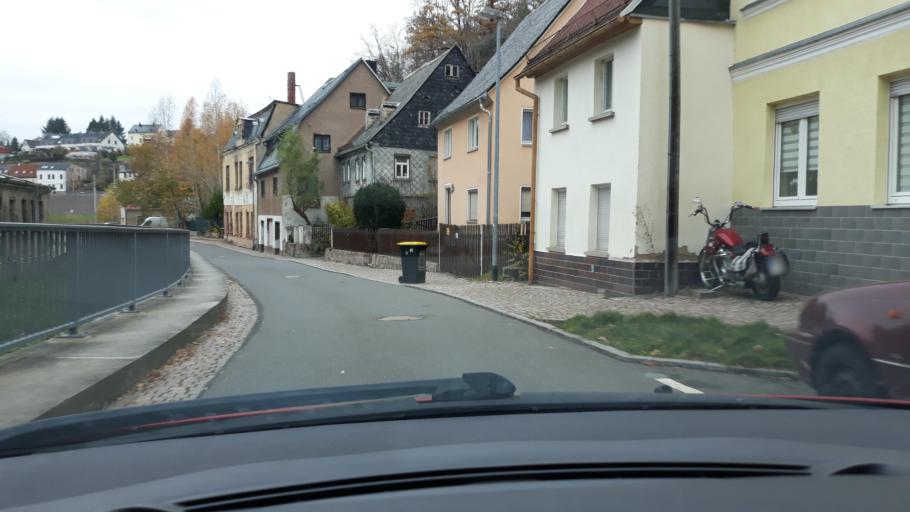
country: DE
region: Saxony
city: Kirchberg
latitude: 50.6214
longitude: 12.5340
